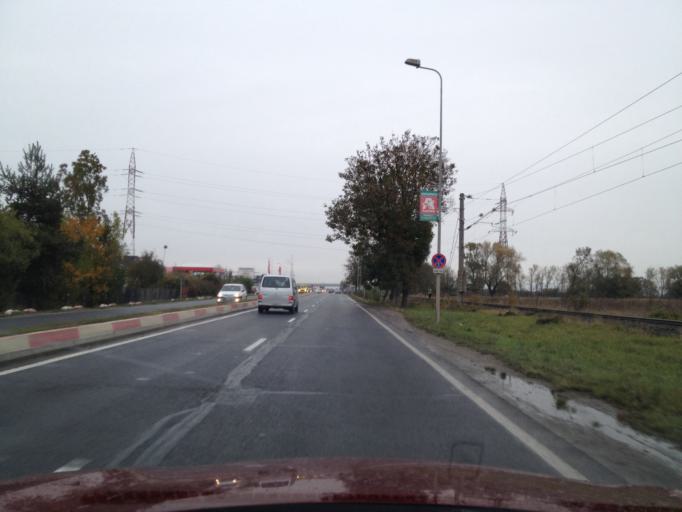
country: RO
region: Brasov
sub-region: Comuna Sanpetru
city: Sanpetru
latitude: 45.6791
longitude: 25.6541
